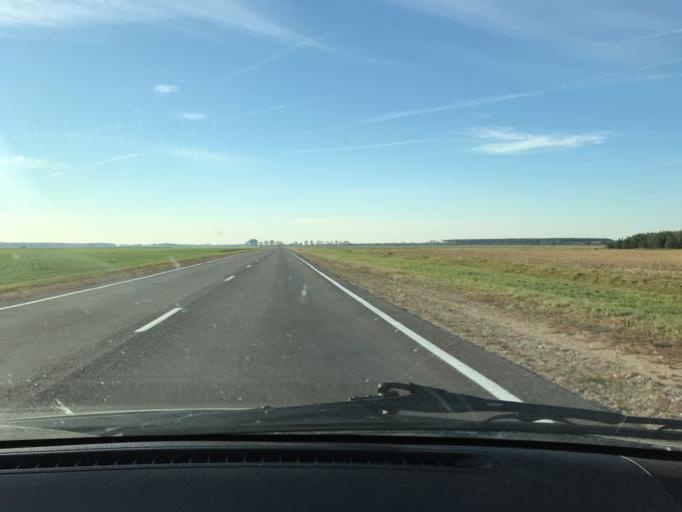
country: BY
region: Brest
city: Antopal'
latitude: 52.2239
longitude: 24.8281
